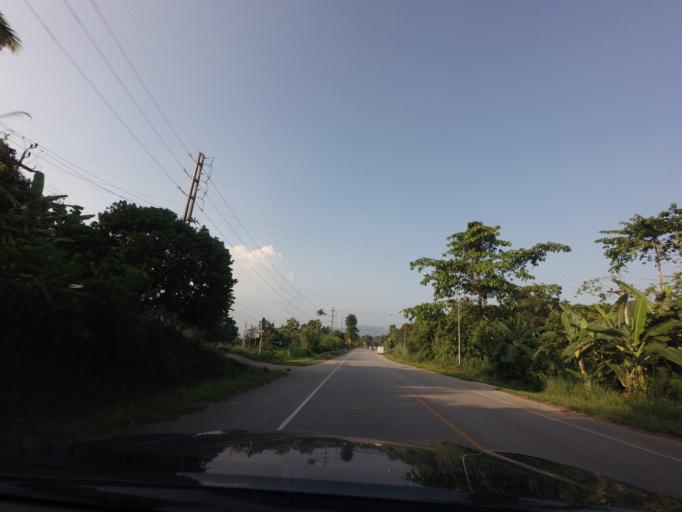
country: TH
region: Loei
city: Dan Sai
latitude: 17.2306
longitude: 101.1501
